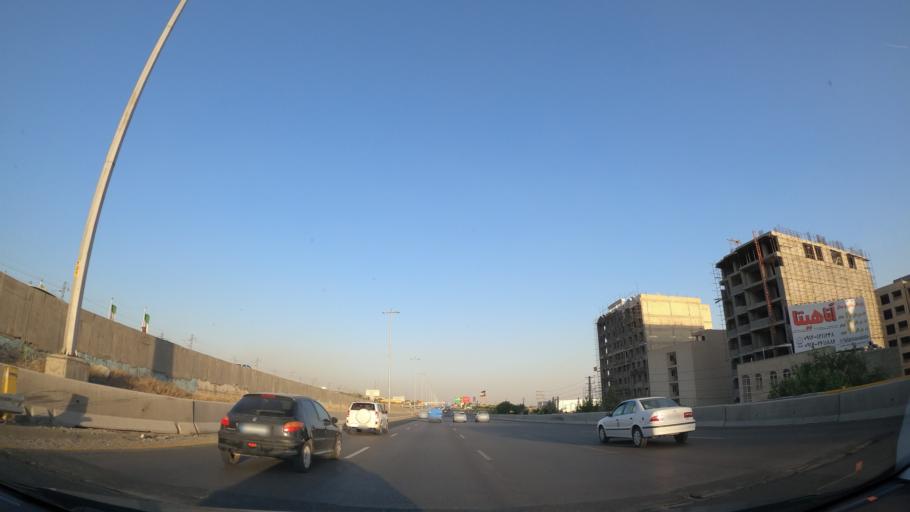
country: IR
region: Tehran
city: Shahr-e Qods
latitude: 35.7561
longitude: 51.0716
